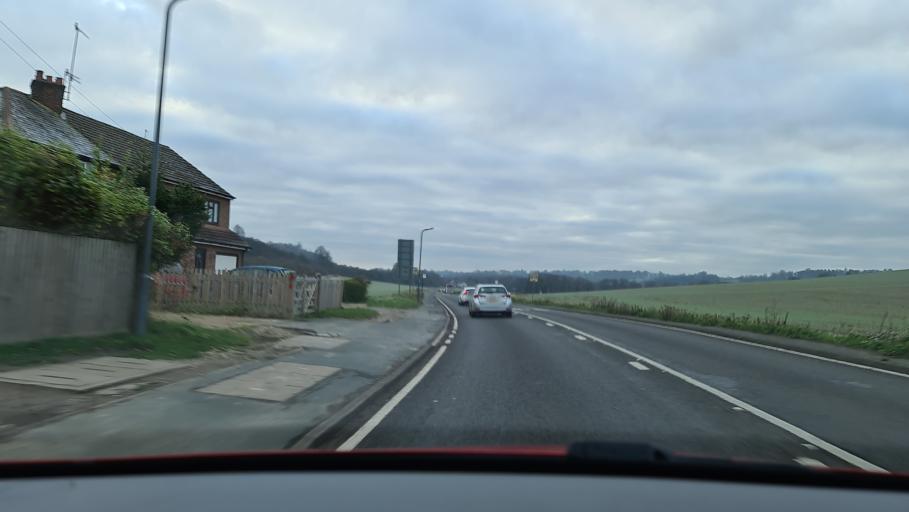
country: GB
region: England
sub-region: Buckinghamshire
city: High Wycombe
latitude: 51.6528
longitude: -0.7996
